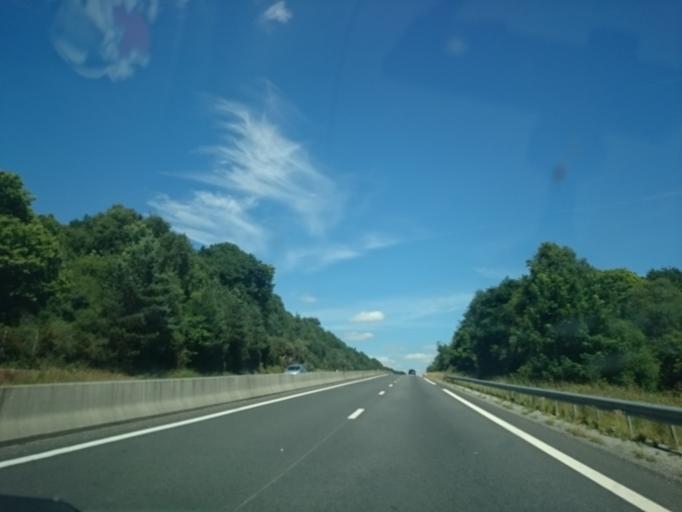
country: FR
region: Brittany
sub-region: Departement des Cotes-d'Armor
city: Mur-de-Bretagne
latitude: 48.2190
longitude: -3.0525
